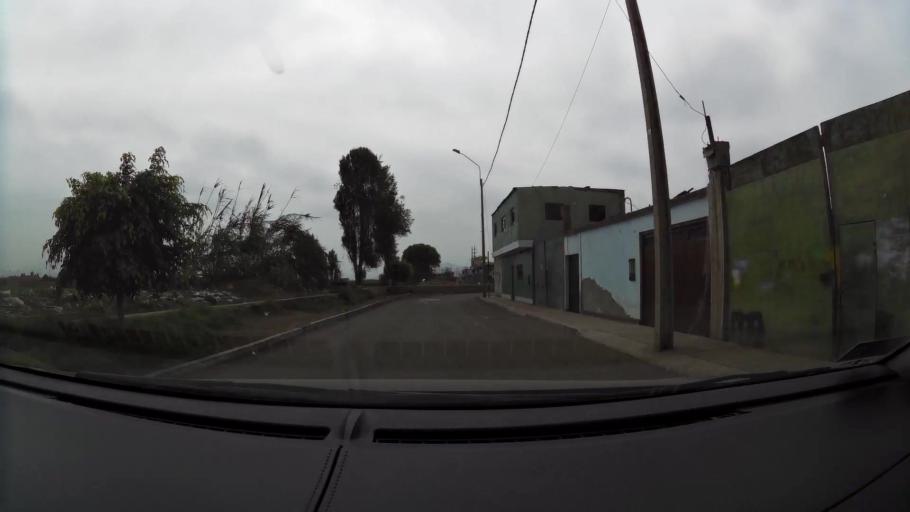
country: PE
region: Lima
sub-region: Provincia de Huaral
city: Huaral
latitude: -11.4946
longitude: -77.2185
